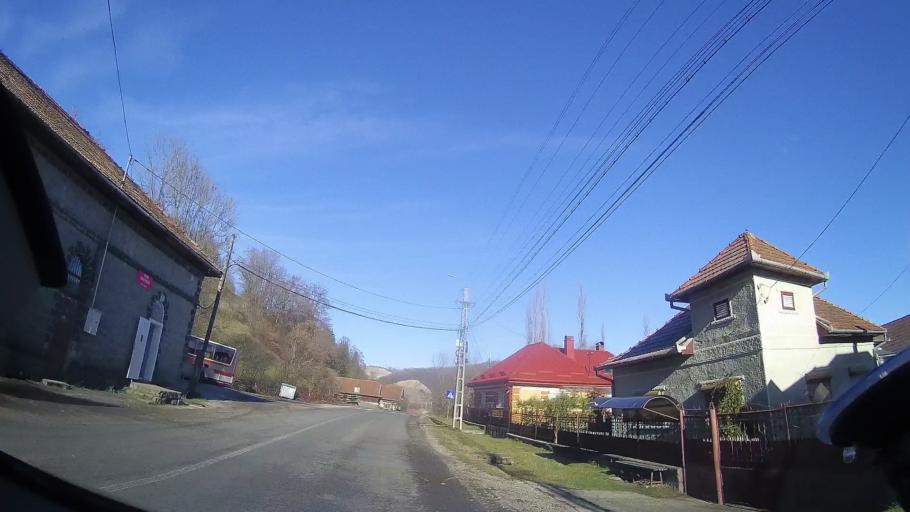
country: RO
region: Cluj
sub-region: Comuna Poeni
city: Poeni
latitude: 46.8819
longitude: 22.8787
